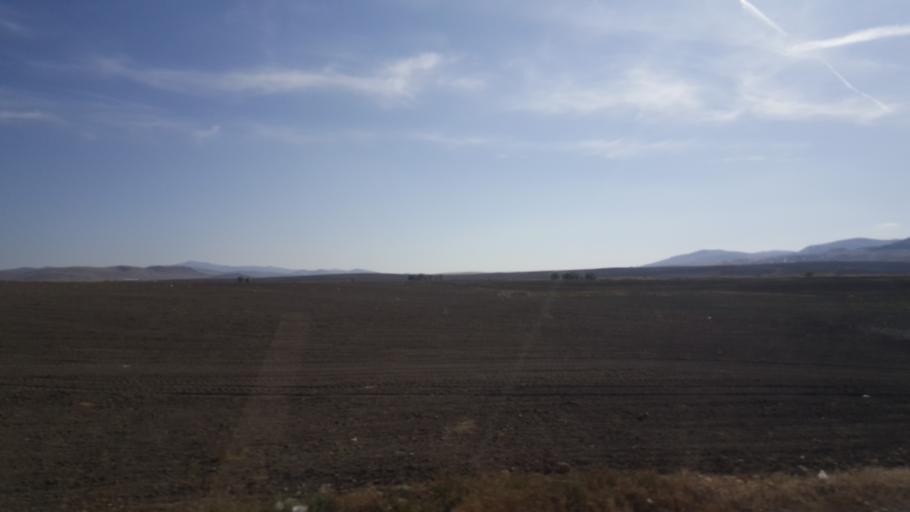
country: TR
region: Ankara
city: Yenice
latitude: 39.3794
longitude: 32.7577
